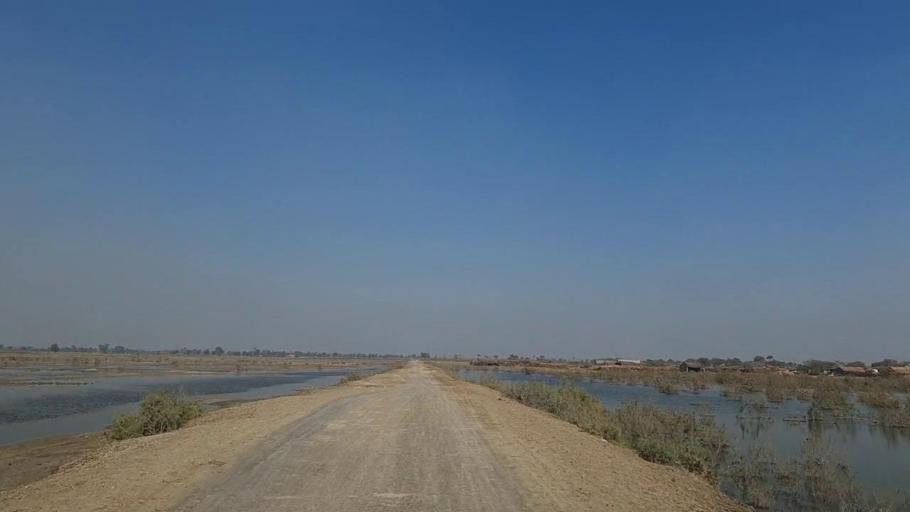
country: PK
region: Sindh
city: Daur
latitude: 26.4742
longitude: 68.3253
